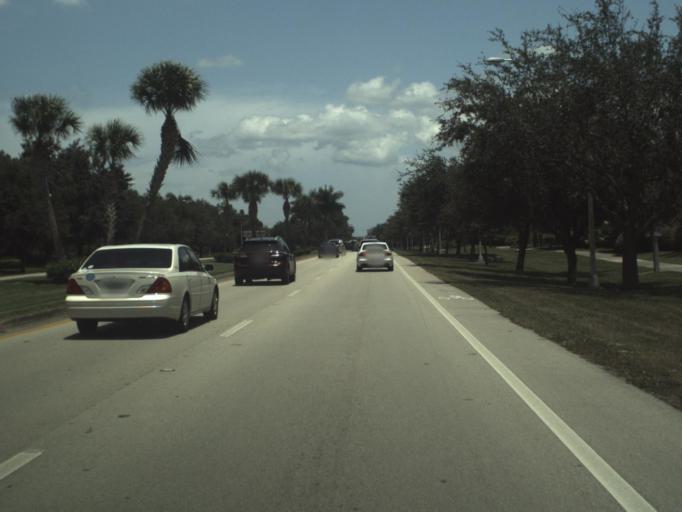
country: US
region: Florida
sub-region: Martin County
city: Palm City
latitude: 27.1722
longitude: -80.2762
